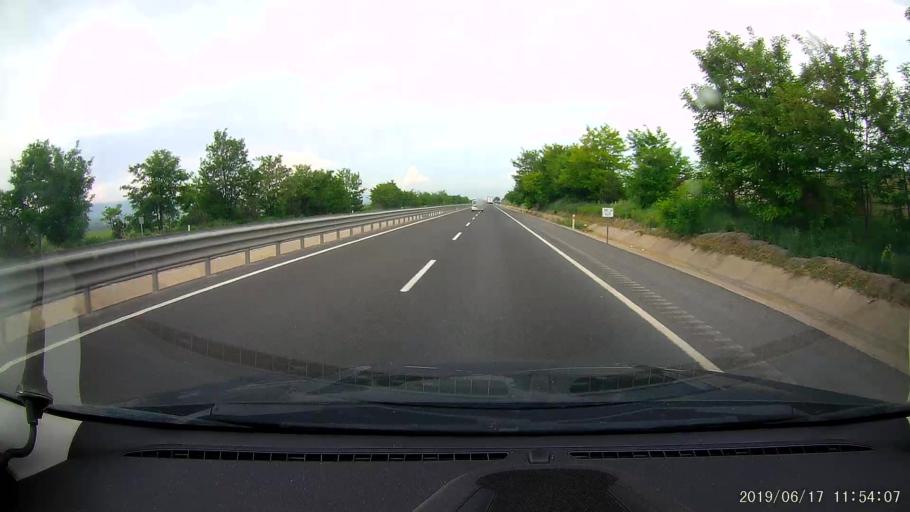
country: TR
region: Cankiri
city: Atkaracalar
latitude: 40.8035
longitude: 33.0393
